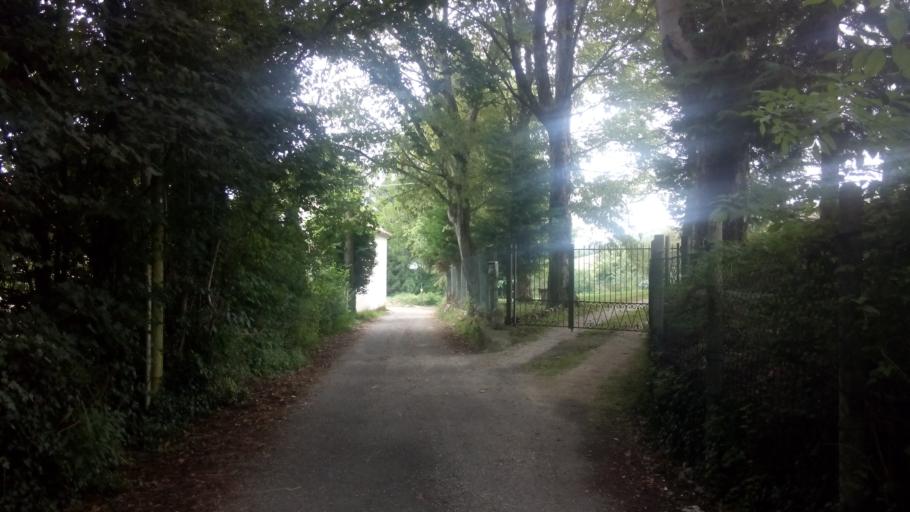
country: IT
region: Veneto
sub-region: Provincia di Vicenza
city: Conco
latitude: 45.7864
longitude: 11.6028
